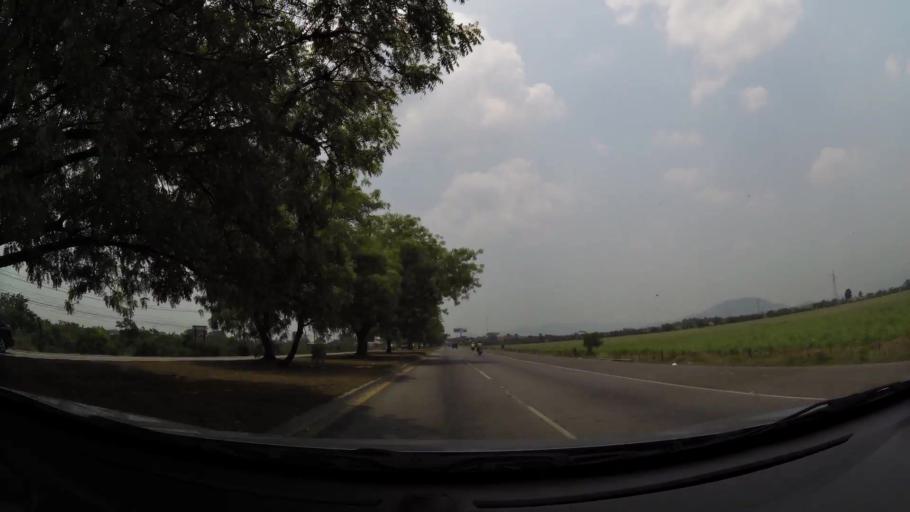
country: HN
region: Cortes
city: La Lima
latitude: 15.4494
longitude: -87.9449
